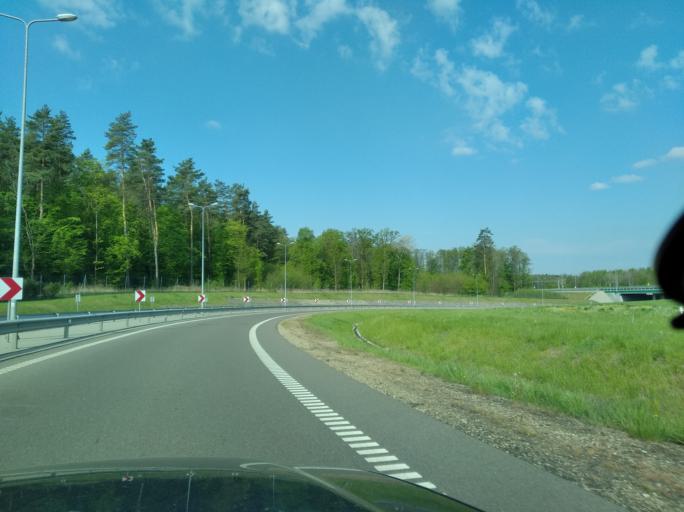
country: PL
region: Subcarpathian Voivodeship
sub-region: Powiat lubaczowski
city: Wielkie Oczy
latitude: 49.9614
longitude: 23.0724
